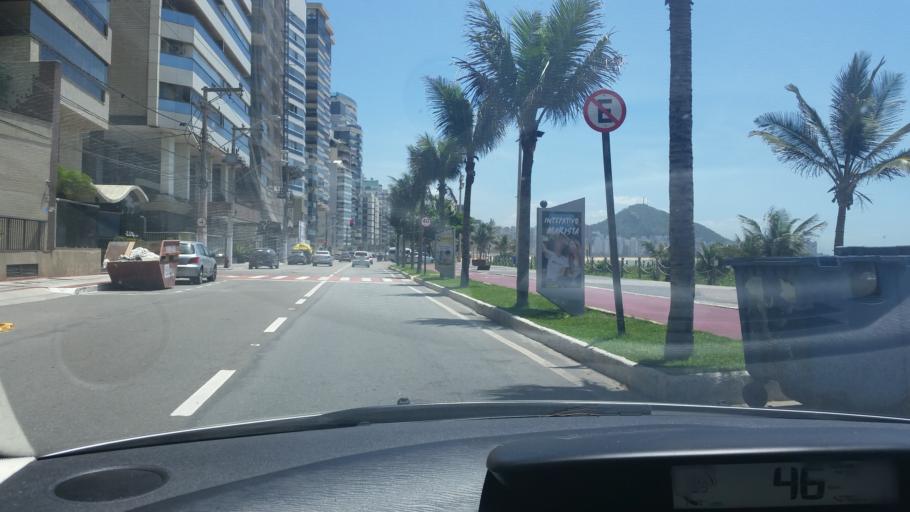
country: BR
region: Espirito Santo
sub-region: Vila Velha
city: Vila Velha
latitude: -20.3500
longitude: -40.2839
